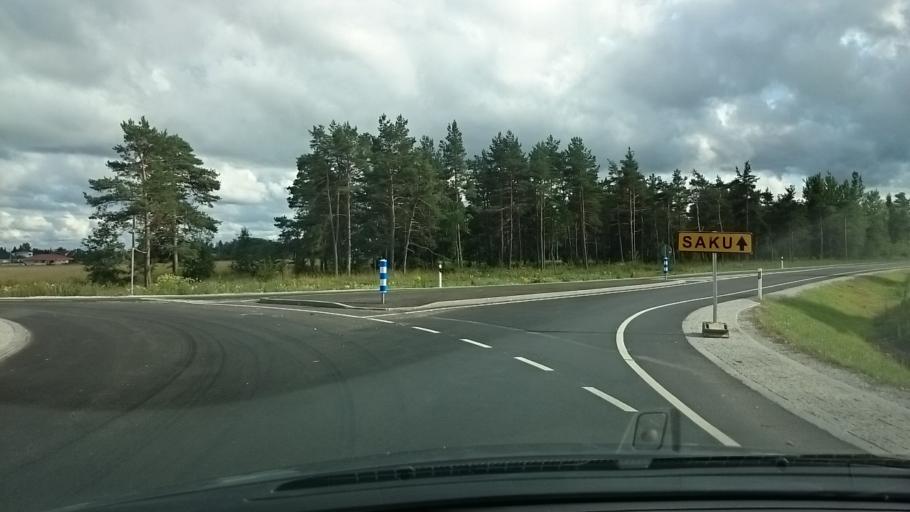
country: EE
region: Harju
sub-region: Saku vald
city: Saku
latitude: 59.3136
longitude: 24.6404
